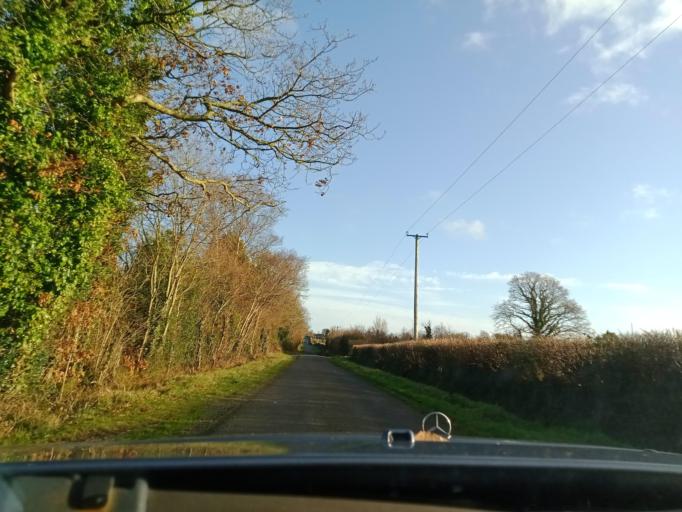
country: IE
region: Leinster
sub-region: Kilkenny
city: Callan
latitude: 52.5008
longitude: -7.4087
